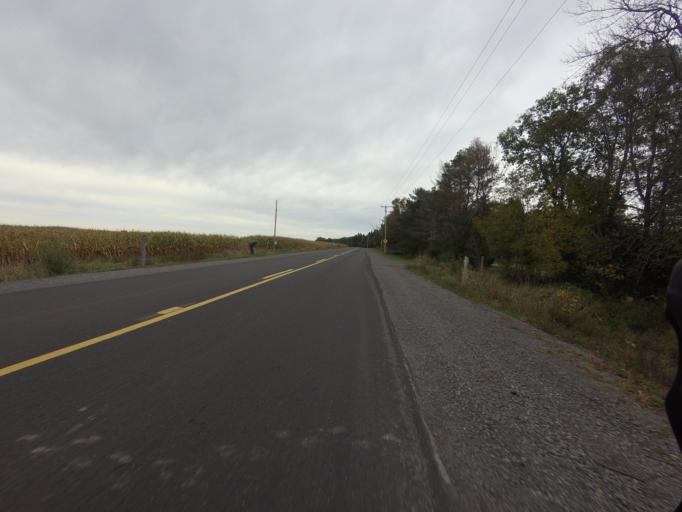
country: CA
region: Ontario
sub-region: Lanark County
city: Smiths Falls
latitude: 44.9892
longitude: -75.7788
